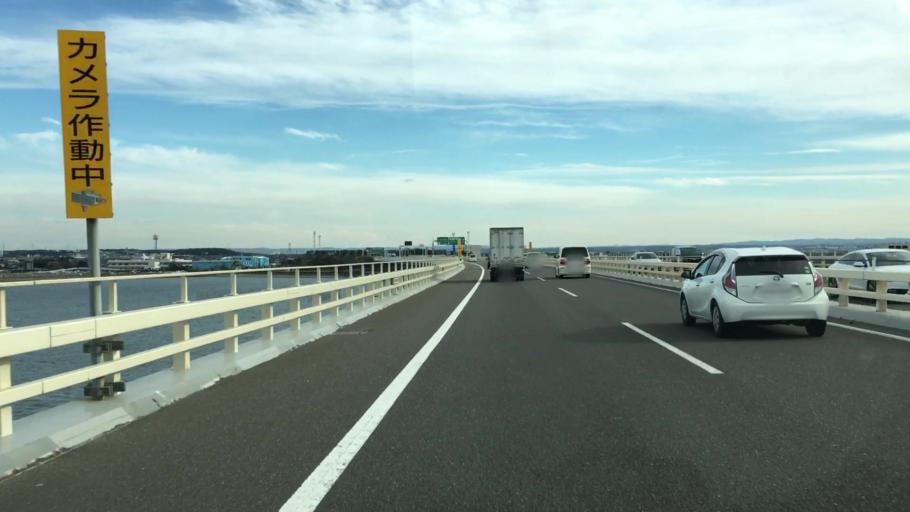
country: JP
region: Chiba
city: Kisarazu
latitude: 35.4397
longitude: 139.9105
